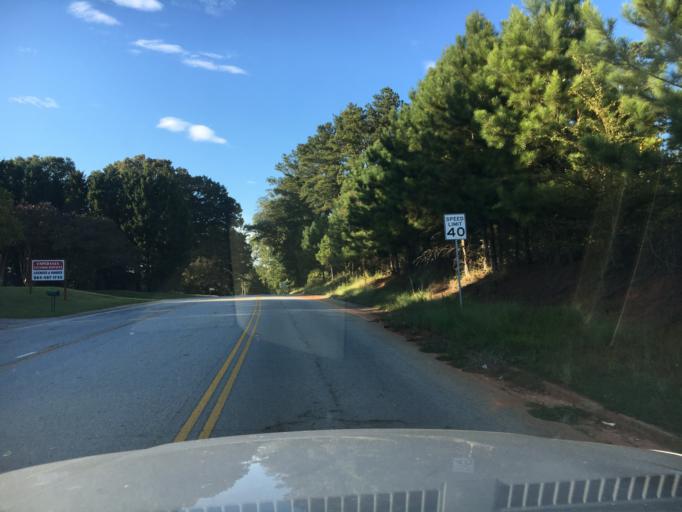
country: US
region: South Carolina
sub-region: Spartanburg County
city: Roebuck
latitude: 34.8788
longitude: -82.0476
